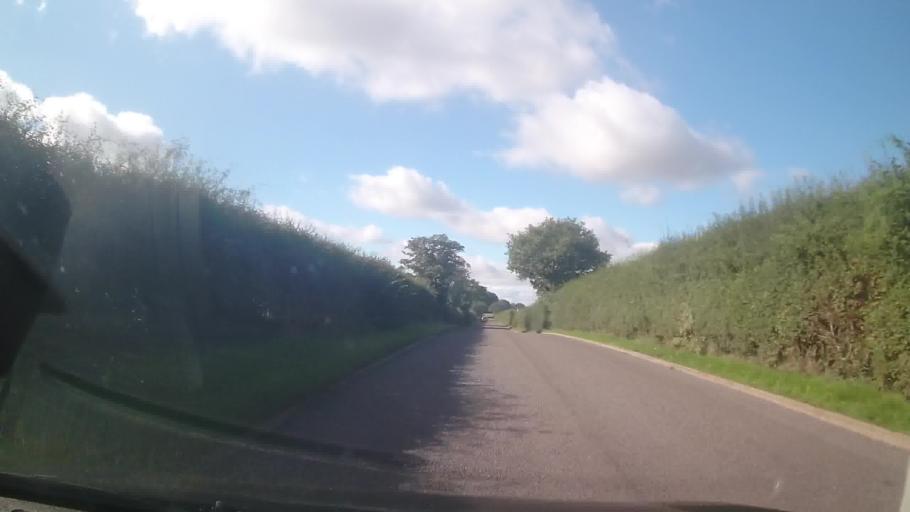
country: GB
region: England
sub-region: Shropshire
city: Bicton
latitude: 52.7509
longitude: -2.8347
